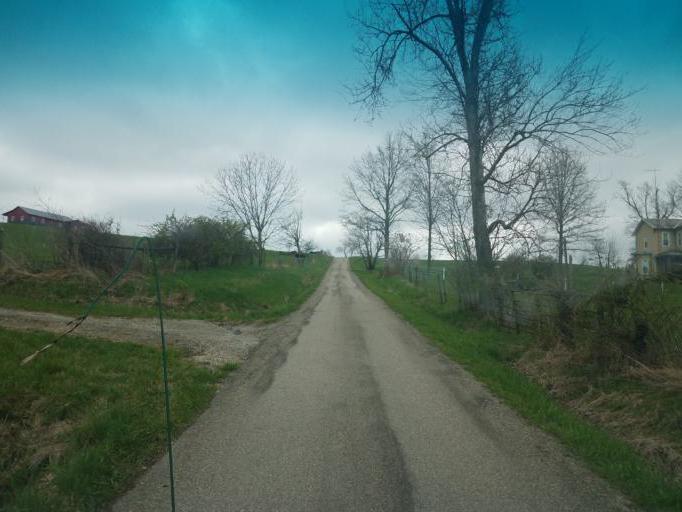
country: US
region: Ohio
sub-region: Stark County
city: Beach City
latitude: 40.6133
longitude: -81.6020
